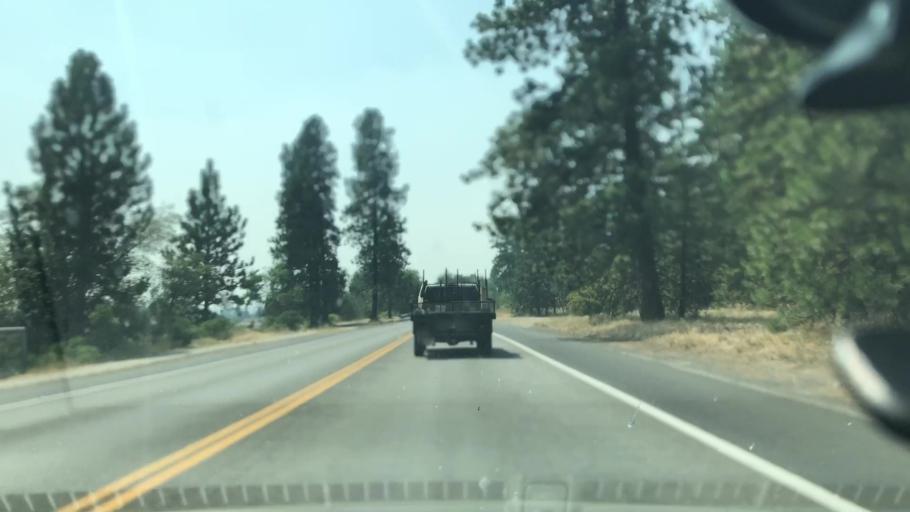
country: US
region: Washington
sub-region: Spokane County
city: Millwood
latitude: 47.6882
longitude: -117.3213
